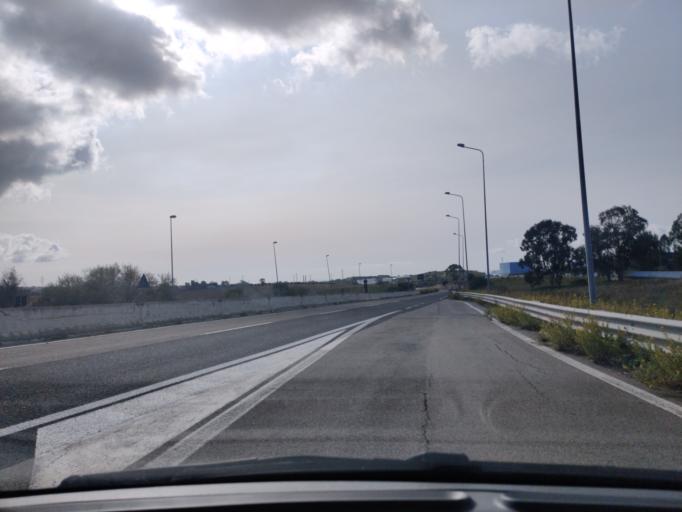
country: IT
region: Latium
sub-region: Citta metropolitana di Roma Capitale
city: Aurelia
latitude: 42.1279
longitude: 11.7917
